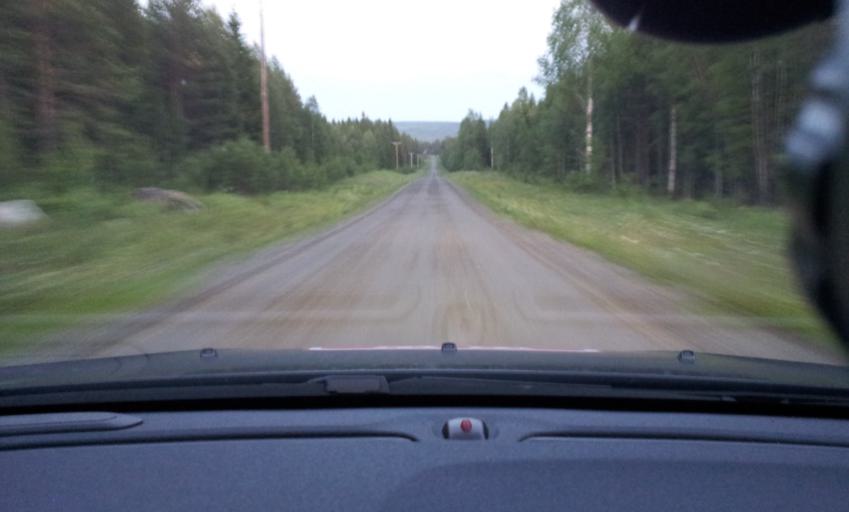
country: SE
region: Vaesternorrland
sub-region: Ange Kommun
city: Fransta
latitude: 62.8068
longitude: 16.0195
